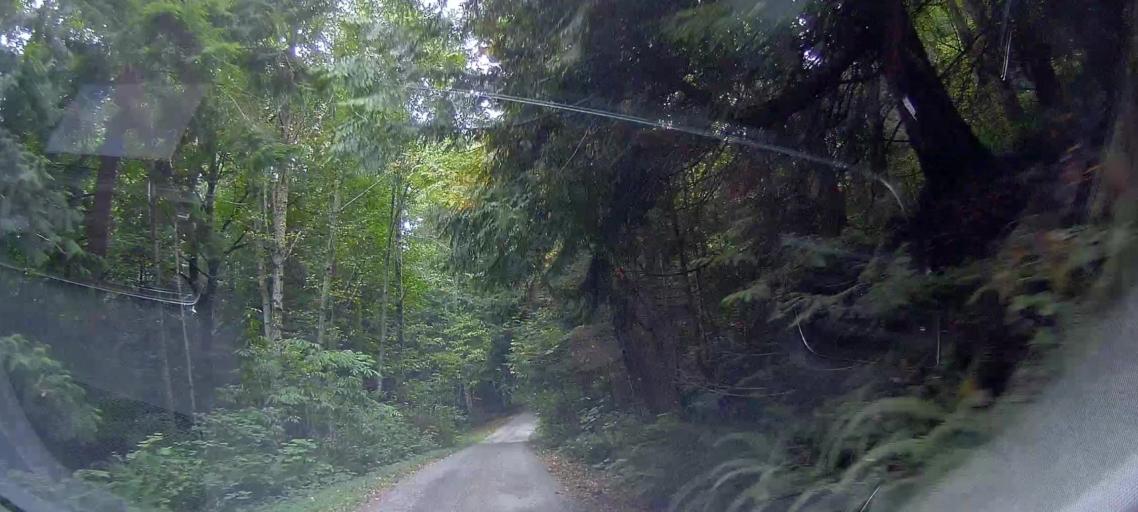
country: US
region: Washington
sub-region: Whatcom County
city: Geneva
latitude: 48.6136
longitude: -122.4360
